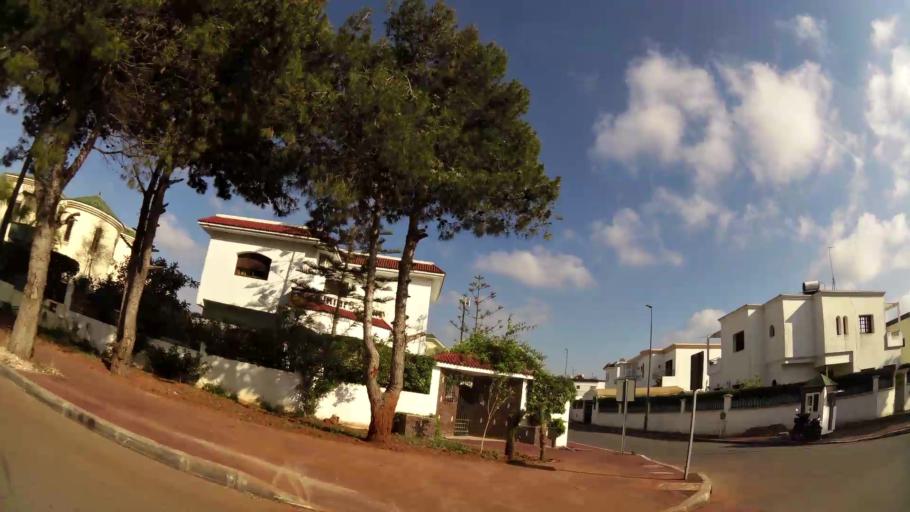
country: MA
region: Rabat-Sale-Zemmour-Zaer
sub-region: Skhirate-Temara
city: Temara
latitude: 33.9498
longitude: -6.8650
